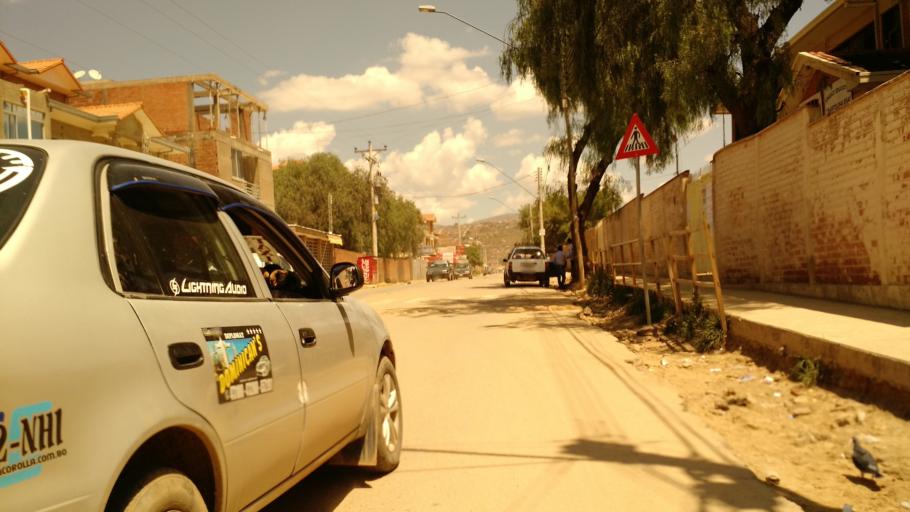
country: BO
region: Cochabamba
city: Cochabamba
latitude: -17.4472
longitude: -66.1555
